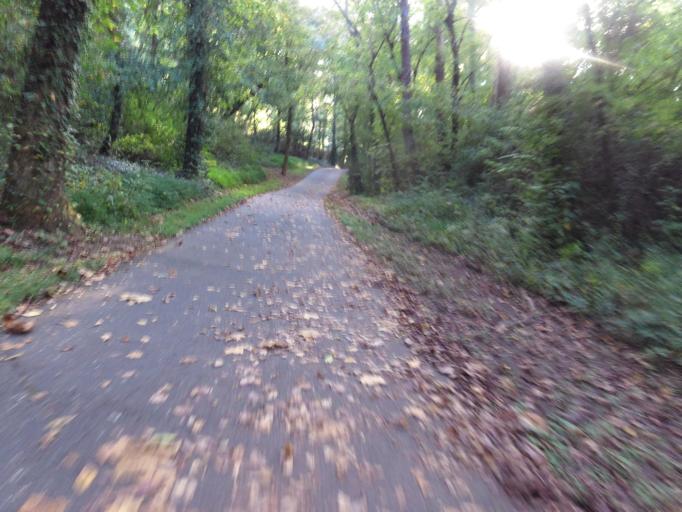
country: US
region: Tennessee
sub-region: Knox County
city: Knoxville
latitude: 35.9470
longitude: -83.9693
